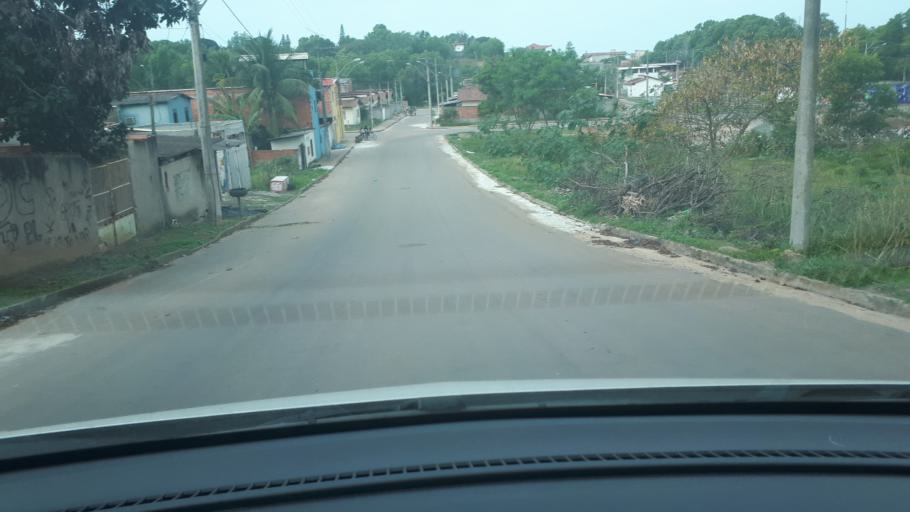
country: BR
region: Espirito Santo
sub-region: Serra
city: Serra
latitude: -20.1446
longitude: -40.1930
